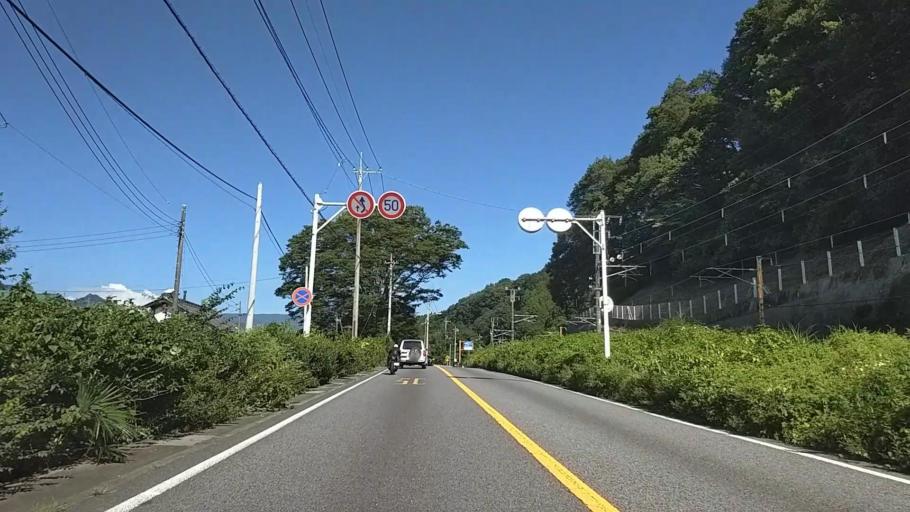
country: JP
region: Gunma
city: Annaka
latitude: 36.3301
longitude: 138.7526
